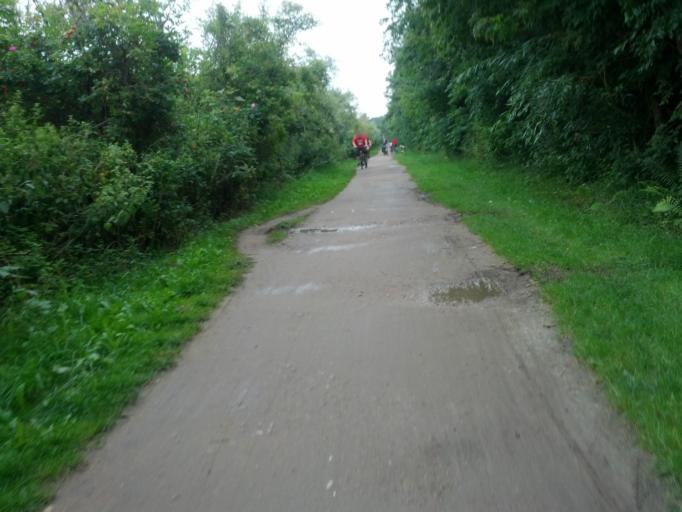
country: DE
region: Mecklenburg-Vorpommern
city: Ostseebad Kuhlungsborn
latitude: 54.1452
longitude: 11.8111
